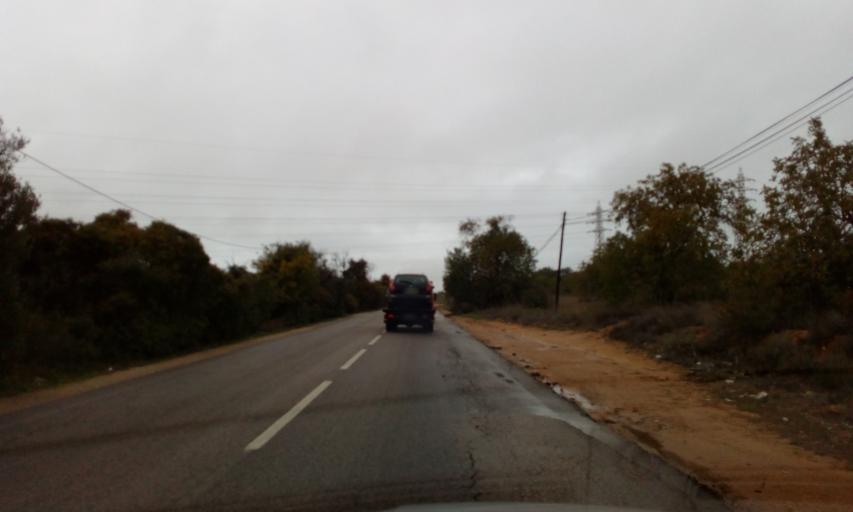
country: PT
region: Faro
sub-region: Albufeira
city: Ferreiras
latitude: 37.1356
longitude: -8.2630
